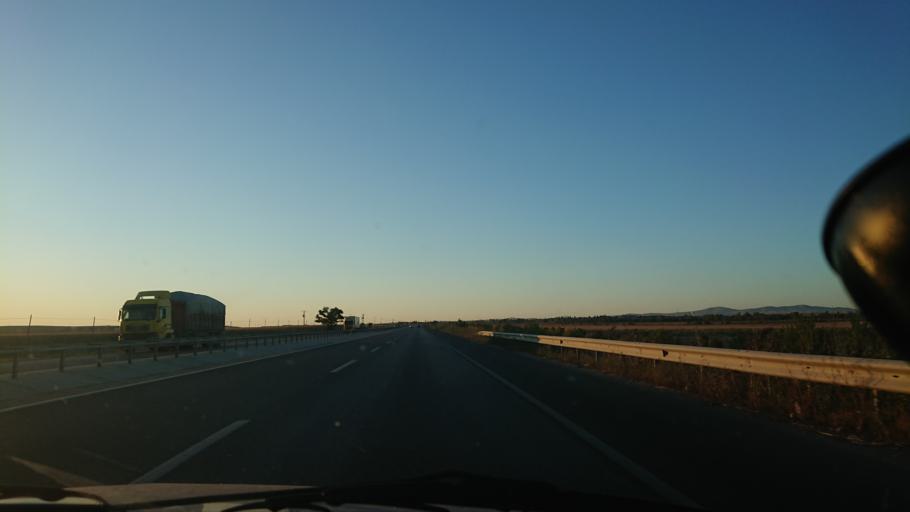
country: TR
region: Eskisehir
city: Mahmudiye
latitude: 39.5473
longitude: 30.9308
